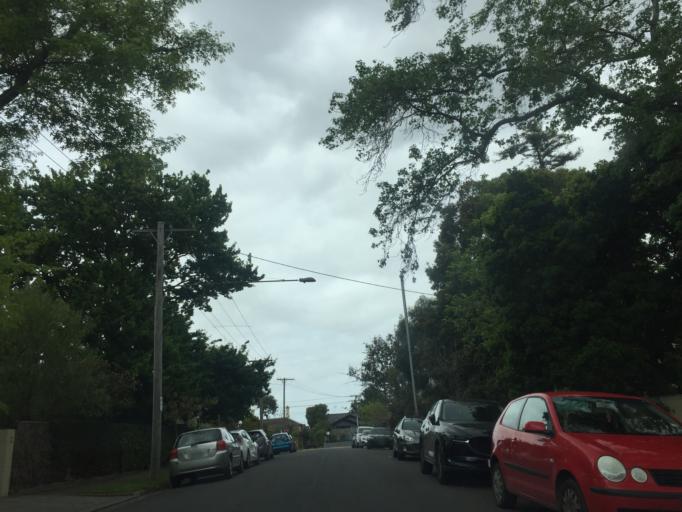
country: AU
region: Victoria
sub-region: Boroondara
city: Kew East
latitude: -37.8078
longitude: 145.0464
